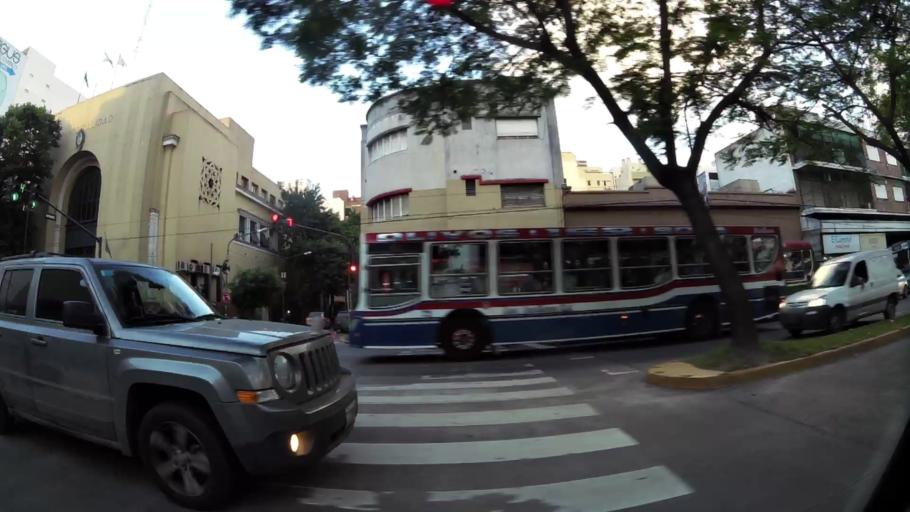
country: AR
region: Buenos Aires
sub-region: Partido de Vicente Lopez
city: Olivos
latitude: -34.5114
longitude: -58.4900
